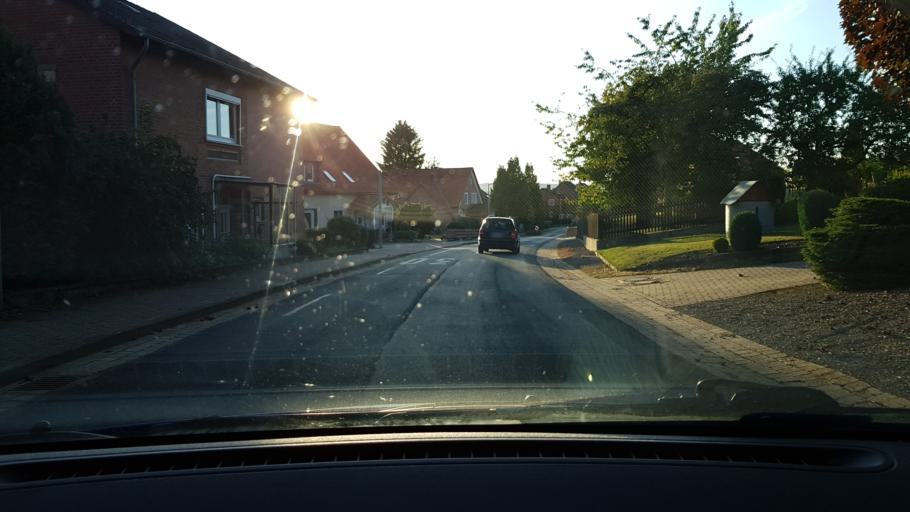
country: DE
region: Lower Saxony
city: Lauenau
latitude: 52.2844
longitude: 9.3853
